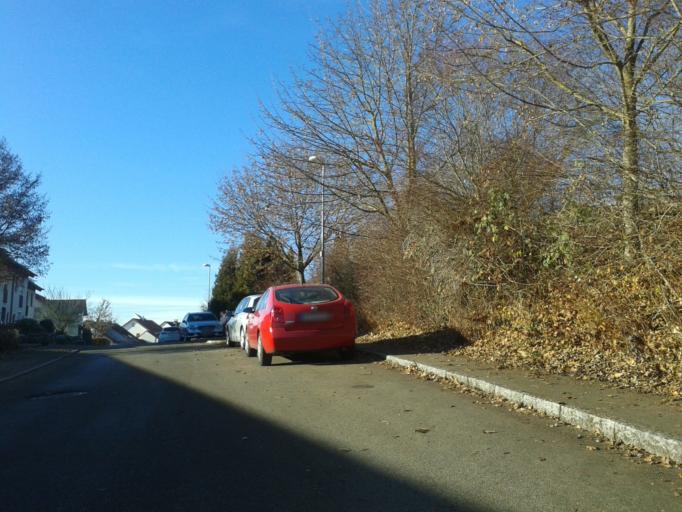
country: DE
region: Baden-Wuerttemberg
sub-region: Tuebingen Region
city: Ulm
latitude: 48.4115
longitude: 9.9477
